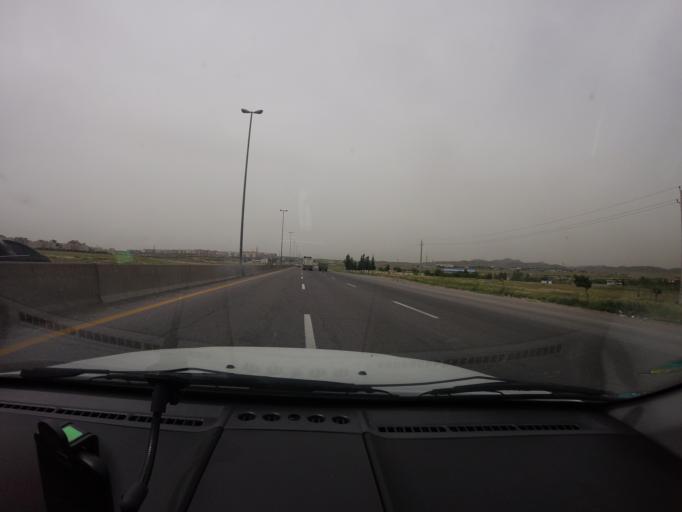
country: IR
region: Tehran
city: Robat Karim
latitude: 35.4980
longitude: 51.0610
